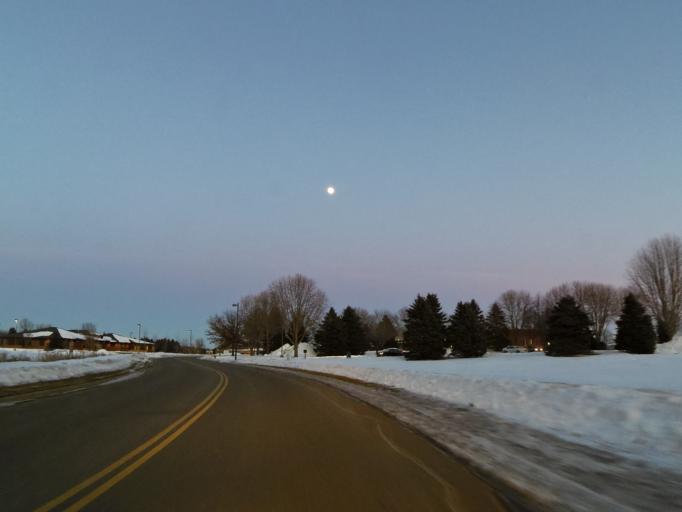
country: US
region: Minnesota
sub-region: Washington County
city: Lake Elmo
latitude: 45.0054
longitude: -92.8776
